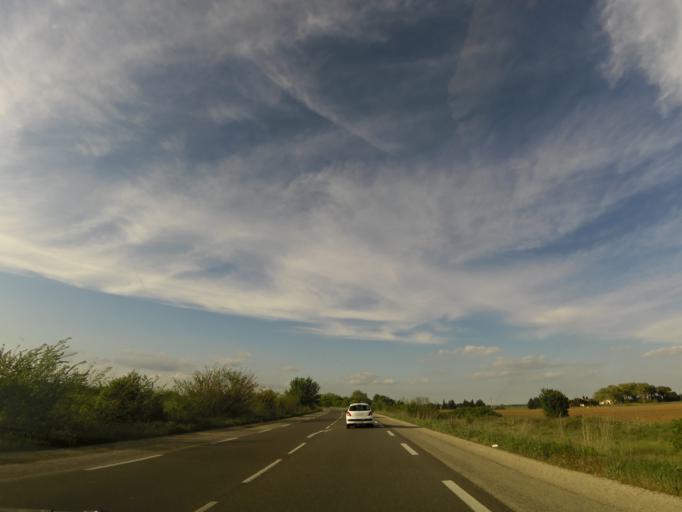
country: FR
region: Languedoc-Roussillon
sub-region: Departement de l'Herault
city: Saint-Just
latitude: 43.6437
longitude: 4.1391
